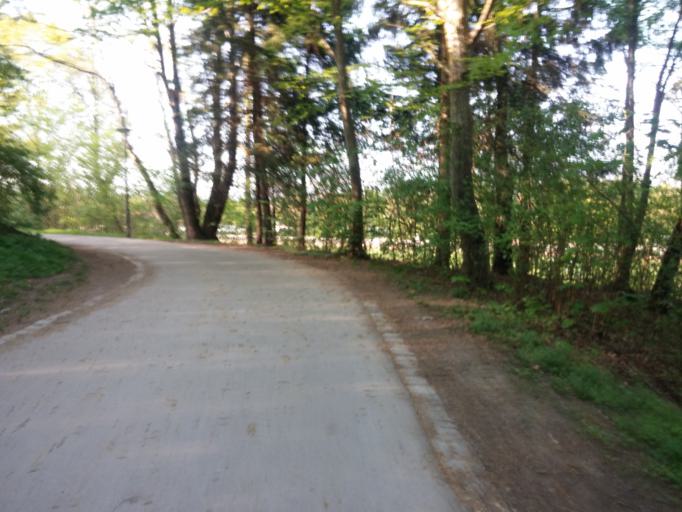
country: DE
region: Bavaria
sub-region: Upper Bavaria
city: Neubiberg
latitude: 48.1116
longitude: 11.6455
